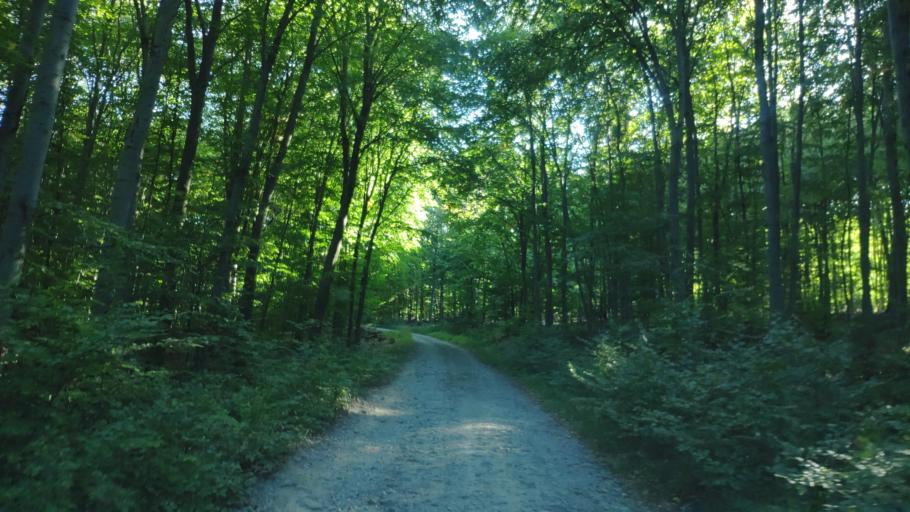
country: SK
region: Presovsky
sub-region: Okres Presov
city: Presov
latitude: 48.8829
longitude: 21.1968
